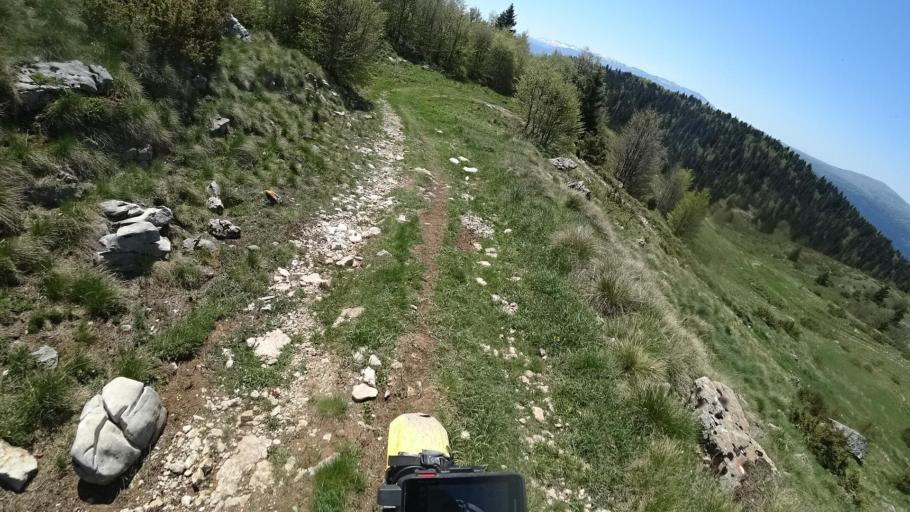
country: BA
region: Federation of Bosnia and Herzegovina
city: Rumboci
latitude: 43.8528
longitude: 17.4553
